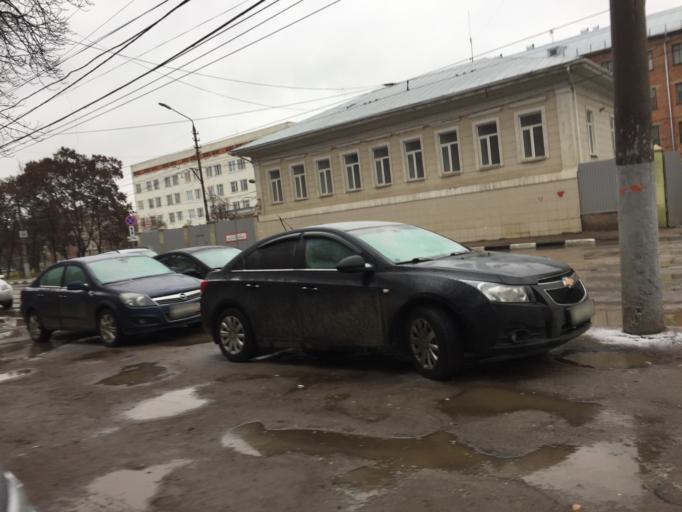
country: RU
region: Tula
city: Tula
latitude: 54.1862
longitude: 37.6240
